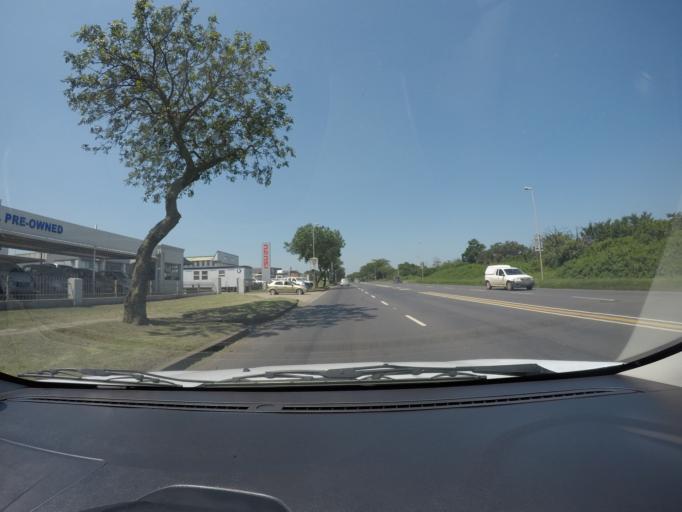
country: ZA
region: KwaZulu-Natal
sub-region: uThungulu District Municipality
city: Richards Bay
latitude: -28.7676
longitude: 32.0162
